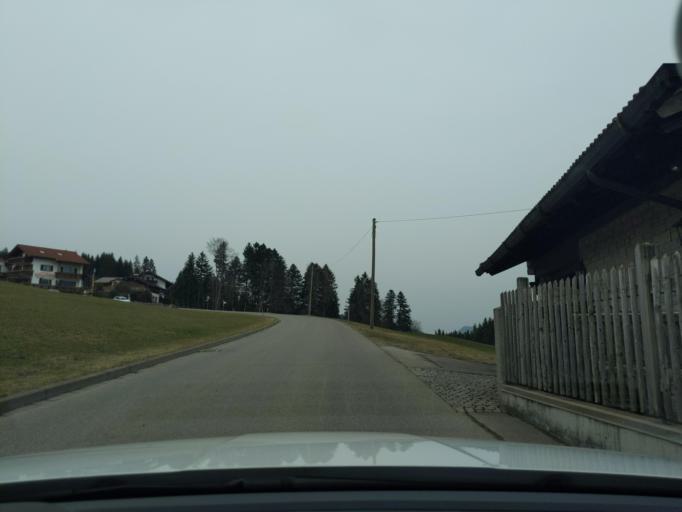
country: DE
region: Bavaria
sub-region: Swabia
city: Ofterschwang
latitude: 47.4945
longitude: 10.2406
